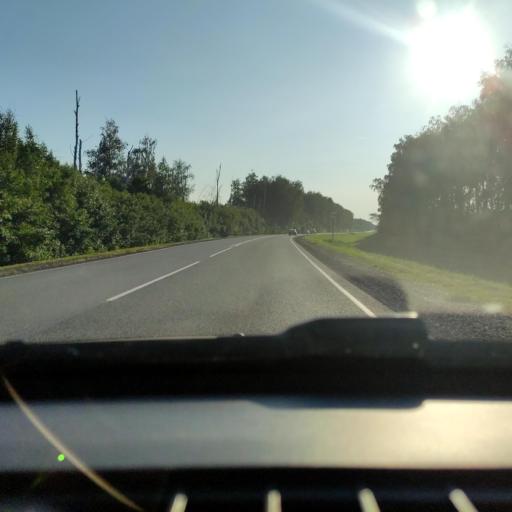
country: RU
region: Voronezj
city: Kashirskoye
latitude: 51.4585
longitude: 39.7696
